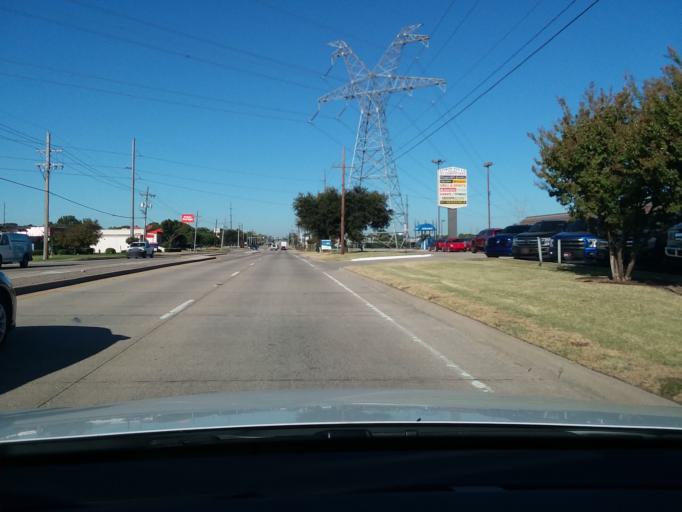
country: US
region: Texas
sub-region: Denton County
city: Highland Village
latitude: 33.0715
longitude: -97.0318
